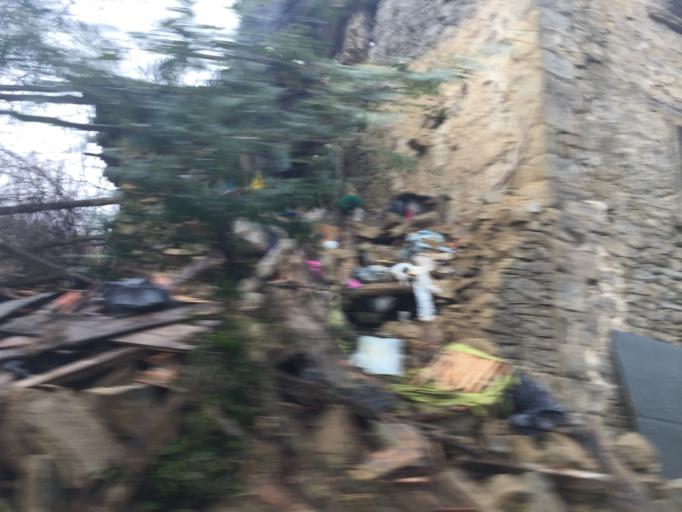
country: IT
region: The Marches
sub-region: Provincia di Ascoli Piceno
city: Arquata del Tronto
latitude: 42.7579
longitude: 13.2965
